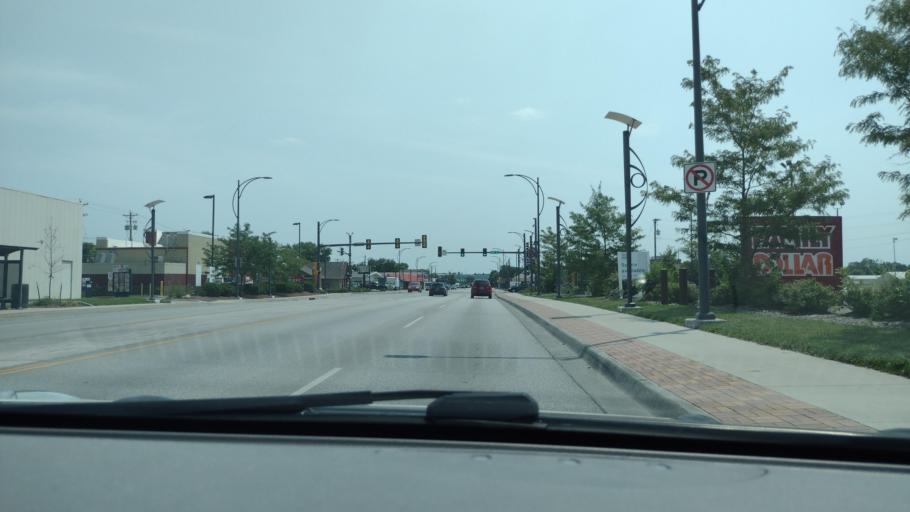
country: US
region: Iowa
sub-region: Pottawattamie County
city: Council Bluffs
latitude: 41.2619
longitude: -95.8901
